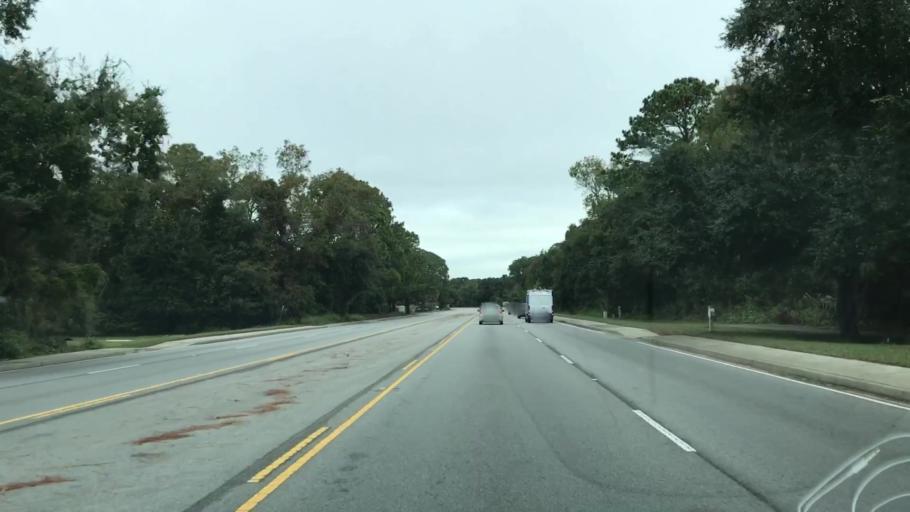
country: US
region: South Carolina
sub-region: Beaufort County
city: Hilton Head Island
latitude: 32.1952
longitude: -80.7042
